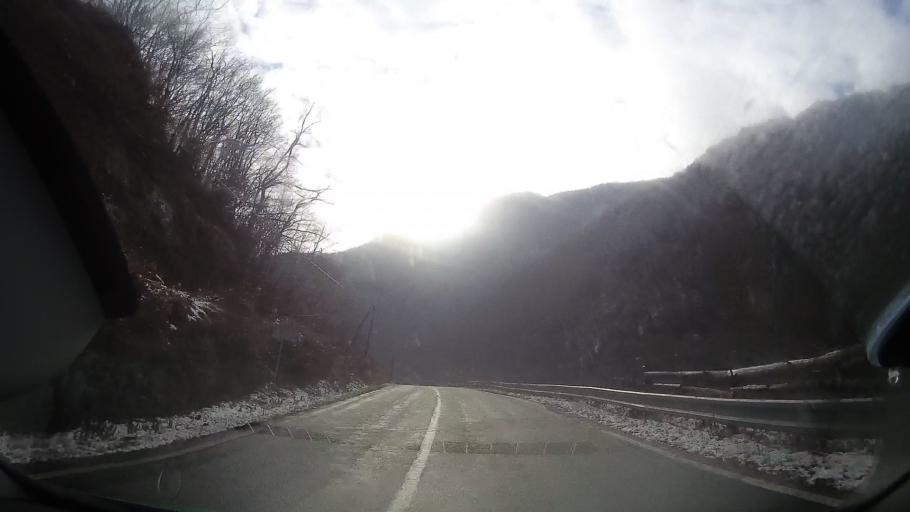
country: RO
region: Alba
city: Salciua de Sus
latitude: 46.4019
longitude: 23.3636
